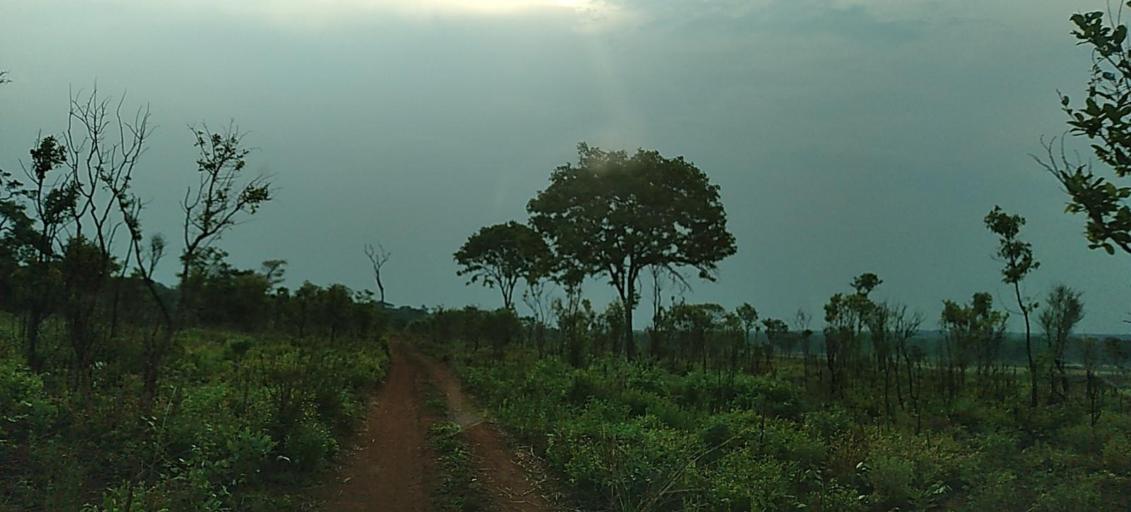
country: ZM
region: North-Western
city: Solwezi
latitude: -12.0428
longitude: 26.0294
